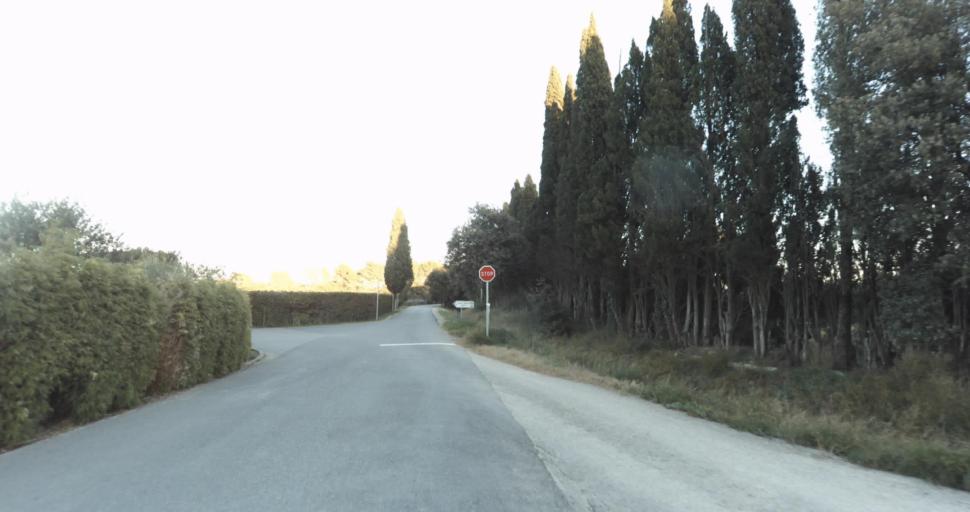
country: FR
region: Provence-Alpes-Cote d'Azur
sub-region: Departement des Bouches-du-Rhone
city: Barbentane
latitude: 43.8836
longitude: 4.7645
